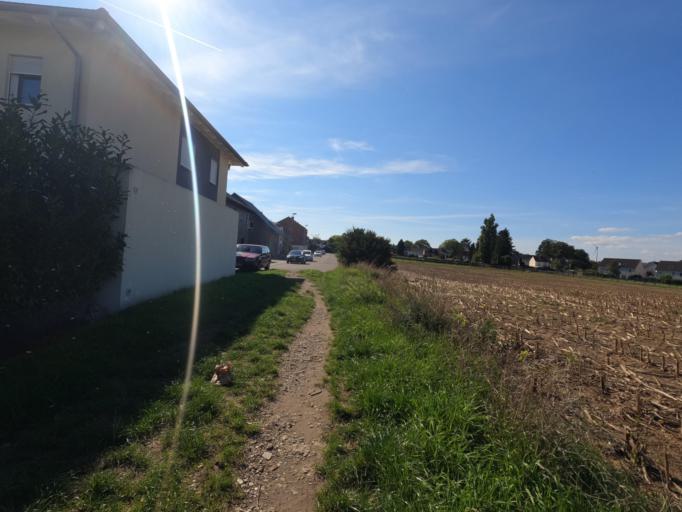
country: DE
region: North Rhine-Westphalia
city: Siersdorf
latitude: 50.8977
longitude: 6.2341
